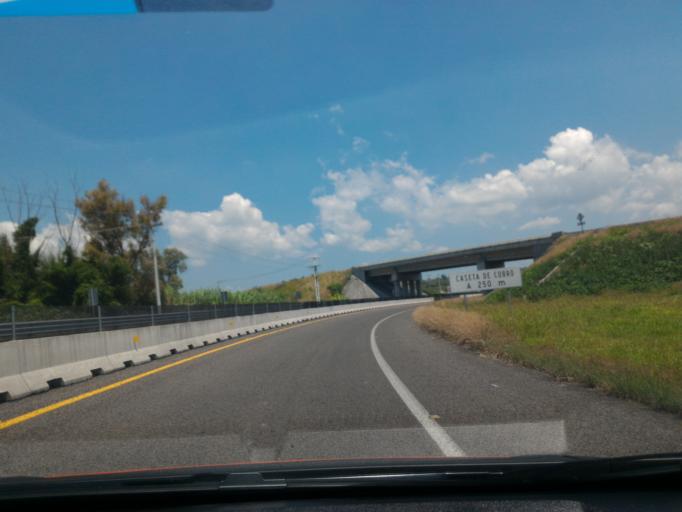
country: MX
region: Guanajuato
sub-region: Penjamo
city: Estacion la Piedad
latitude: 20.3940
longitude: -102.0005
